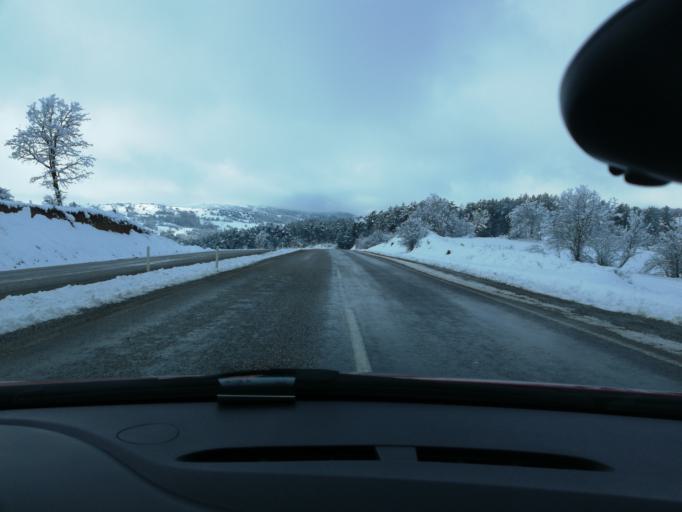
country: TR
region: Kastamonu
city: Ihsangazi
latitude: 41.3138
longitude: 33.5995
